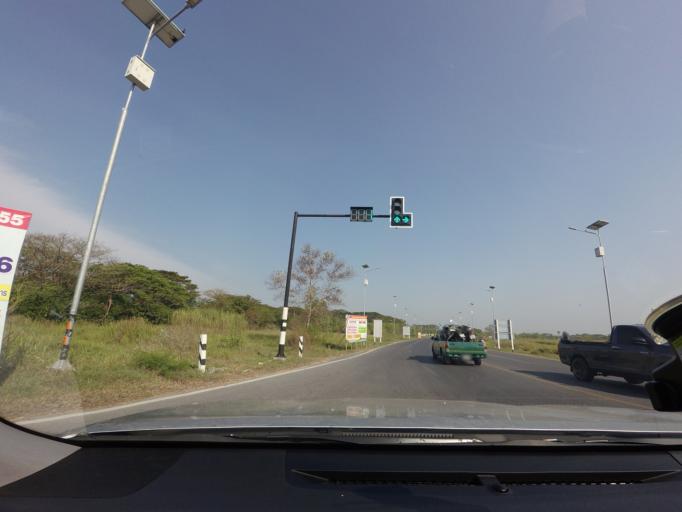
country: TH
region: Nakhon Si Thammarat
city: Nakhon Si Thammarat
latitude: 8.4534
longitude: 99.9801
